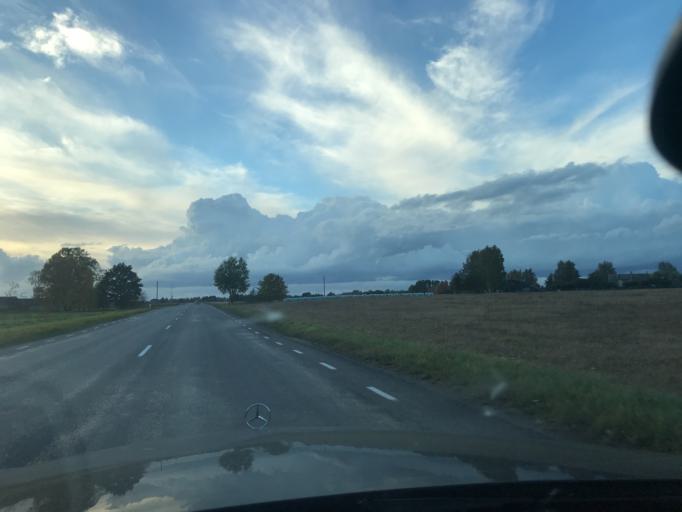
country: EE
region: Vorumaa
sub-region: Antsla vald
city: Vana-Antsla
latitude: 57.8863
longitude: 26.5211
